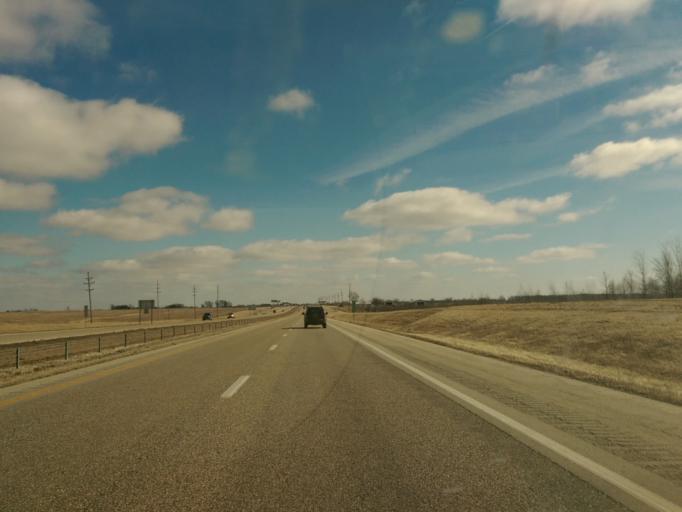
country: US
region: Missouri
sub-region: Montgomery County
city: Montgomery City
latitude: 38.8925
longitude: -91.4316
